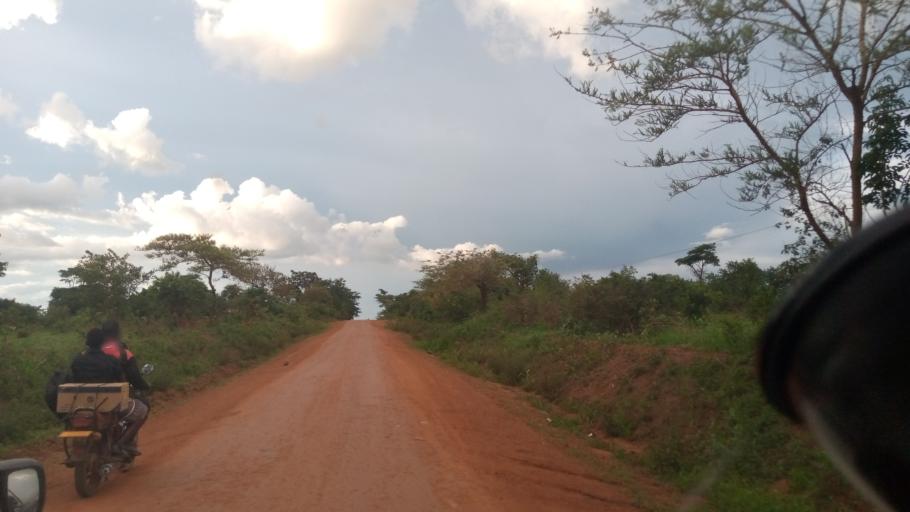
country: UG
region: Northern Region
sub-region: Kole District
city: Kole
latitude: 2.3883
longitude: 32.9332
